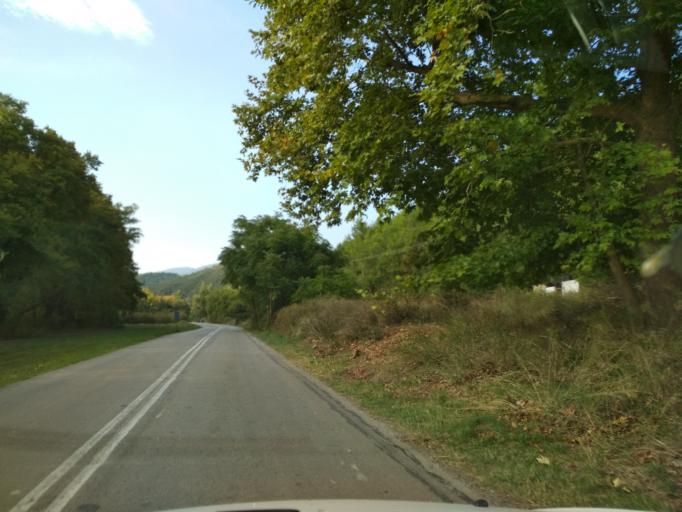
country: GR
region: Central Greece
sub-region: Nomos Evvoias
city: Mantoudi
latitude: 38.7825
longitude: 23.4703
